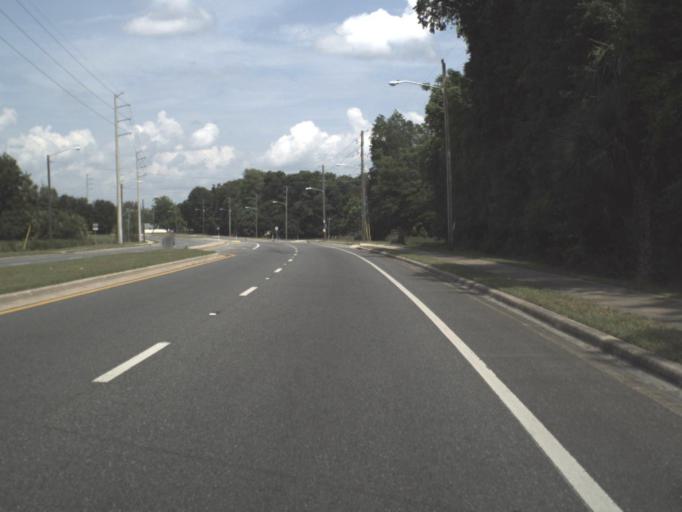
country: US
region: Florida
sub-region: Putnam County
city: Palatka
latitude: 29.6298
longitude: -81.7266
